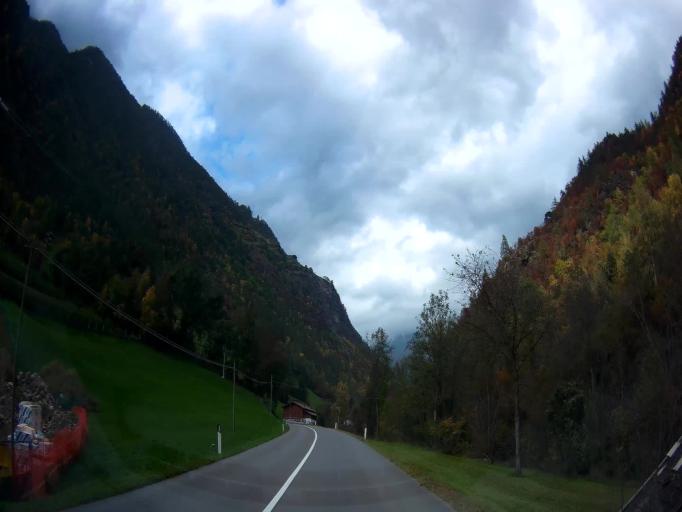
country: IT
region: Trentino-Alto Adige
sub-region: Bolzano
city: Certosa
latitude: 46.6722
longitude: 10.9426
